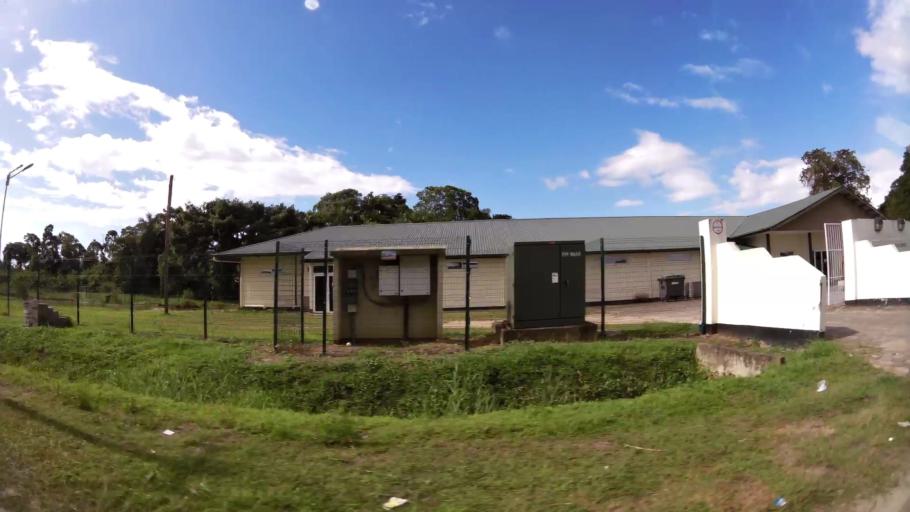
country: SR
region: Paramaribo
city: Paramaribo
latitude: 5.8380
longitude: -55.1598
